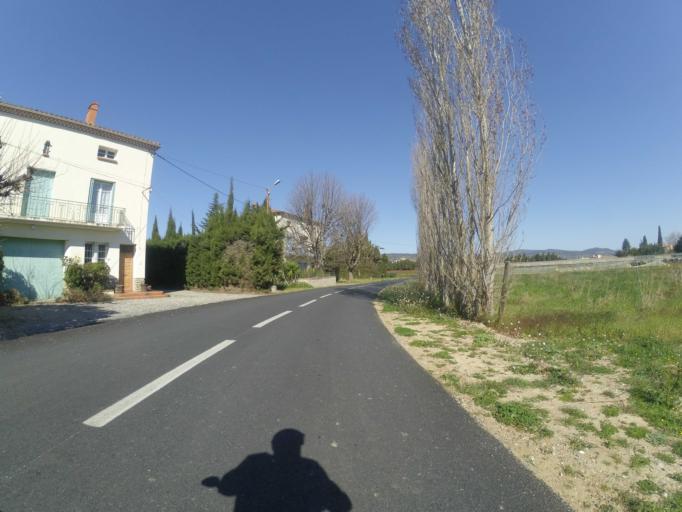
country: FR
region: Languedoc-Roussillon
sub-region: Departement des Pyrenees-Orientales
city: Ille-sur-Tet
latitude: 42.6570
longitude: 2.6213
